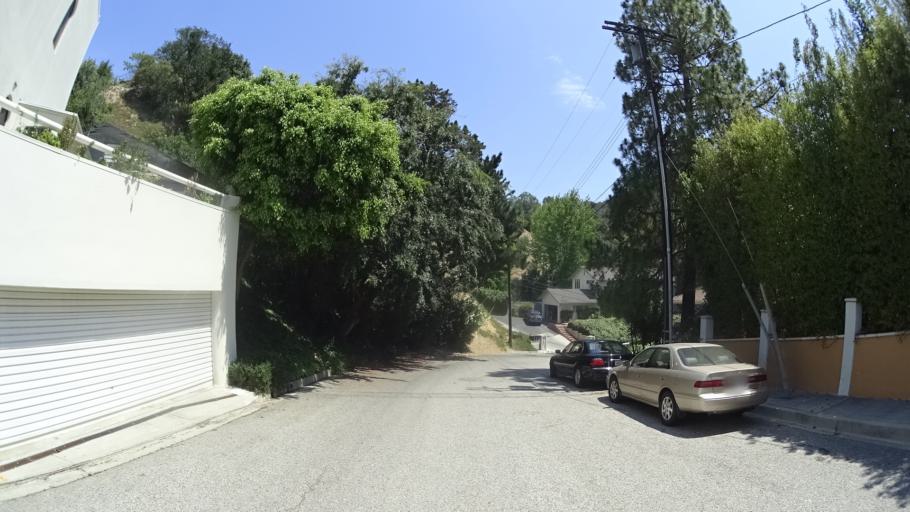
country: US
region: California
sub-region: Los Angeles County
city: Sherman Oaks
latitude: 34.1294
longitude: -118.4162
